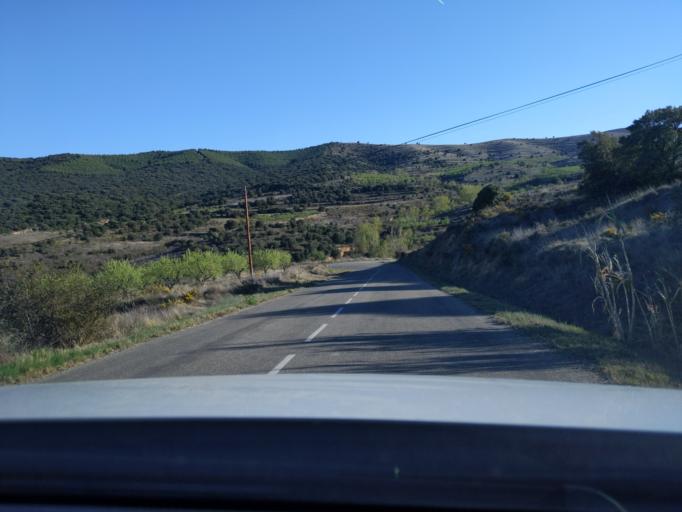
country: ES
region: La Rioja
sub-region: Provincia de La Rioja
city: Bergasillas Bajera
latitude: 42.2461
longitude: -2.1453
